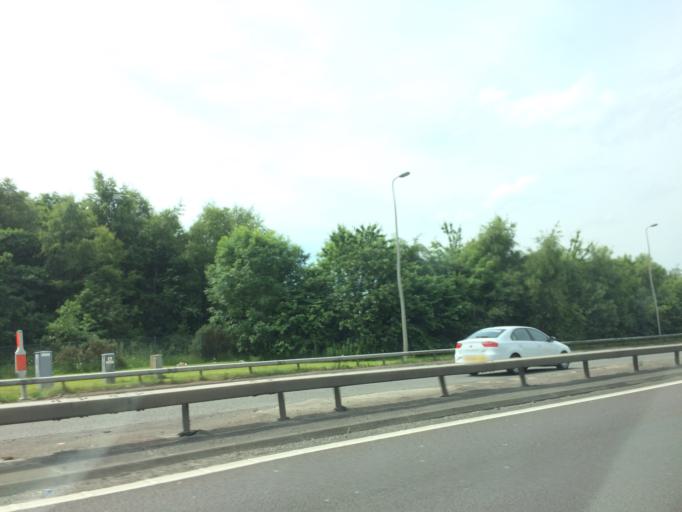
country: GB
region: Scotland
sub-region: East Renfrewshire
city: Giffnock
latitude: 55.8163
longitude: -4.3355
